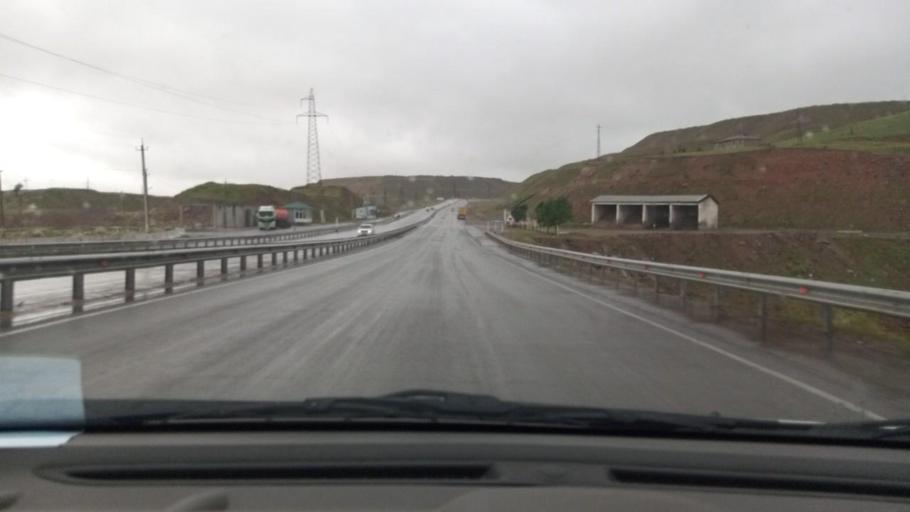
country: UZ
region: Toshkent
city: Angren
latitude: 41.0619
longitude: 70.2078
